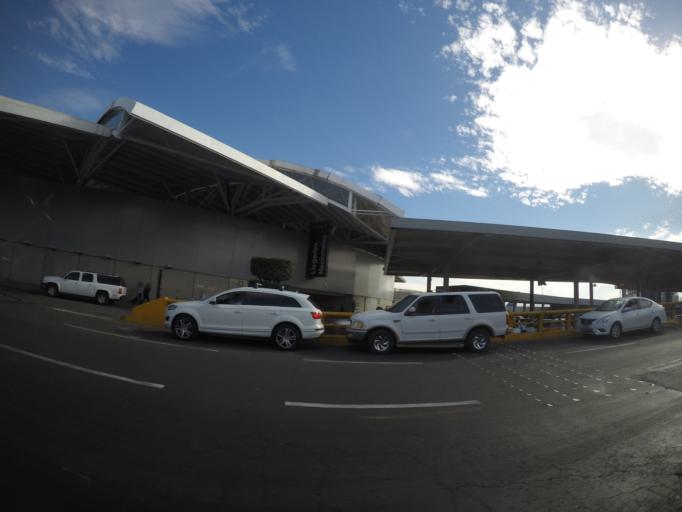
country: MX
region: Mexico City
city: Venustiano Carranza
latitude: 19.4339
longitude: -99.0864
